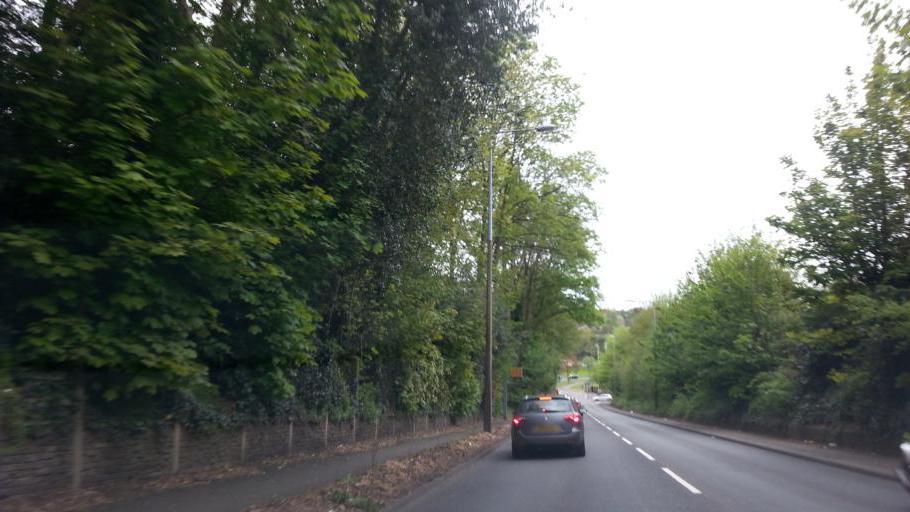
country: GB
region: England
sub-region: Sandwell
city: Cradley Heath
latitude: 52.4558
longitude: -2.0764
